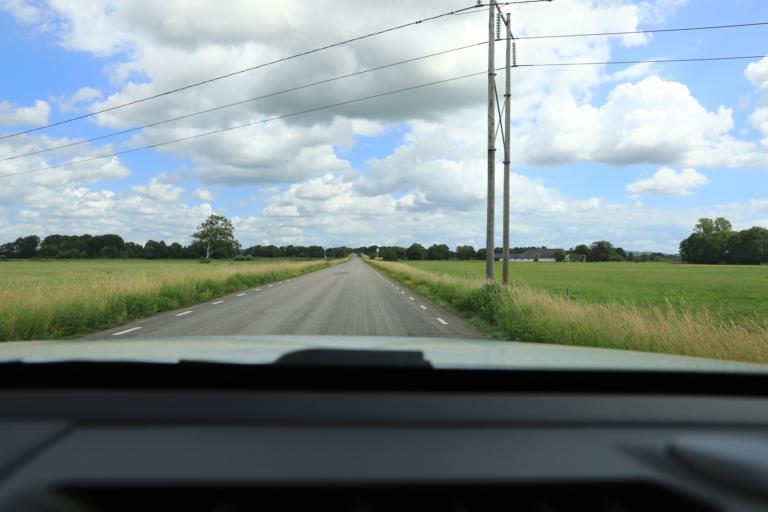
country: SE
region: Halland
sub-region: Varbergs Kommun
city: Tvaaker
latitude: 57.0243
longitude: 12.3794
